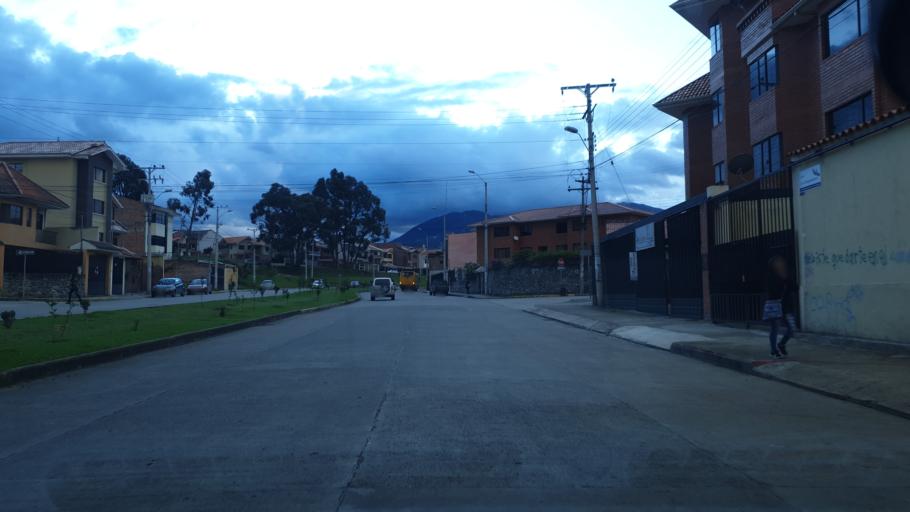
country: EC
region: Azuay
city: Cuenca
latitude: -2.9160
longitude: -79.0292
